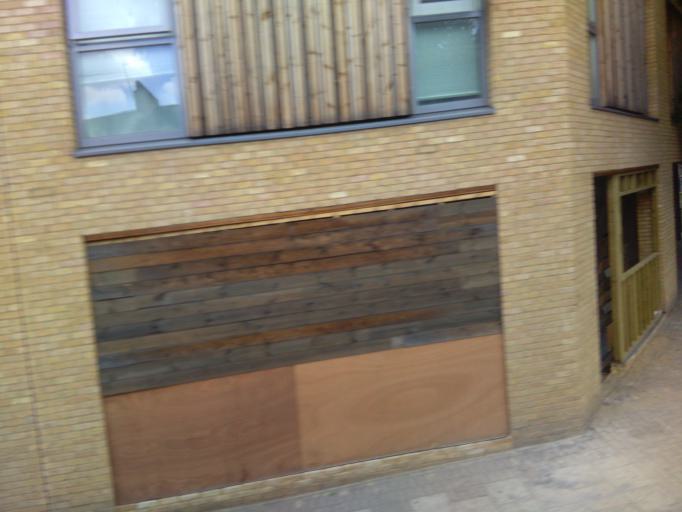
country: GB
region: England
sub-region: Greater London
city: Kennington
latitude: 51.4799
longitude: -0.1071
